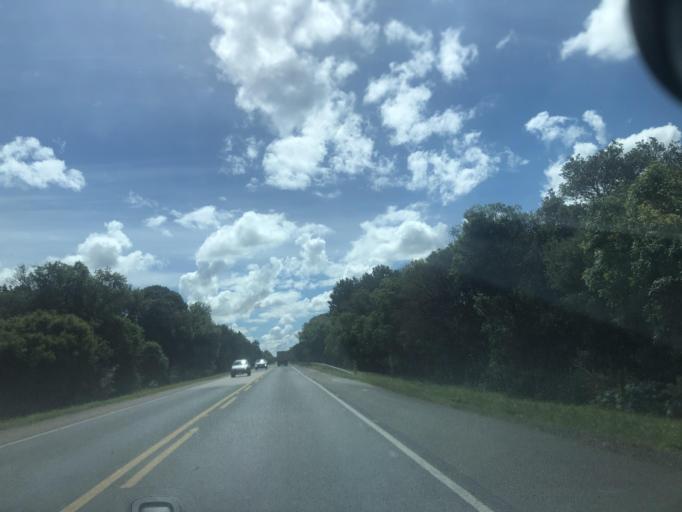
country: BR
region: Santa Catarina
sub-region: Tres Barras
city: Tres Barras
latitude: -26.3374
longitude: -50.0752
